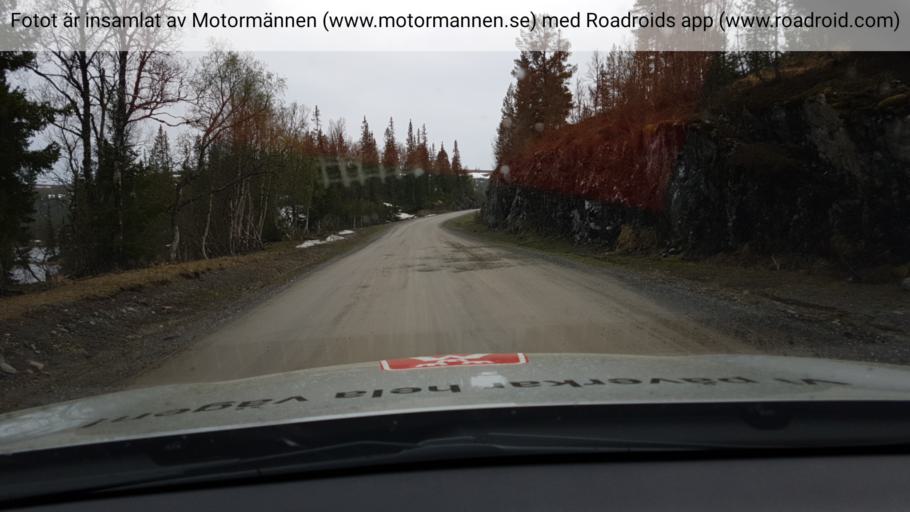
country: NO
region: Nord-Trondelag
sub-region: Snasa
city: Snaase
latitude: 63.6930
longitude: 12.3147
